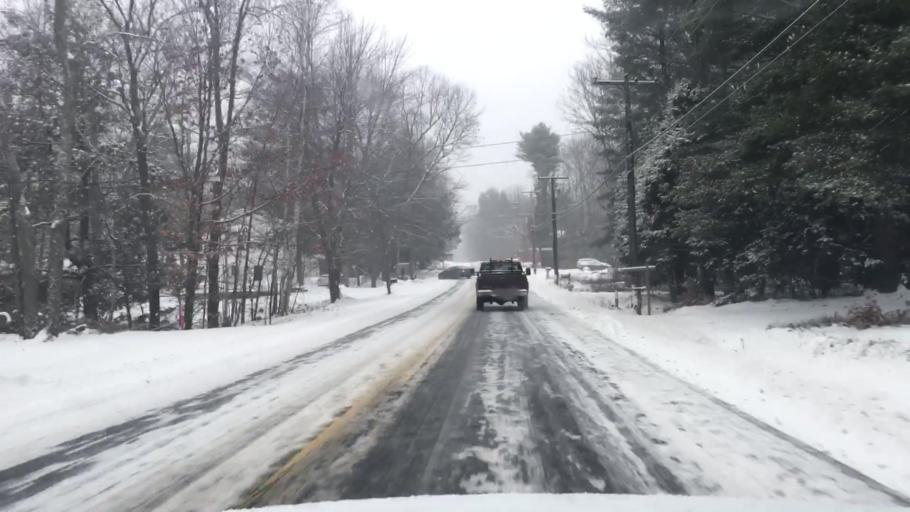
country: US
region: Maine
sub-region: Cumberland County
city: Cumberland Center
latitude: 43.8255
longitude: -70.3167
